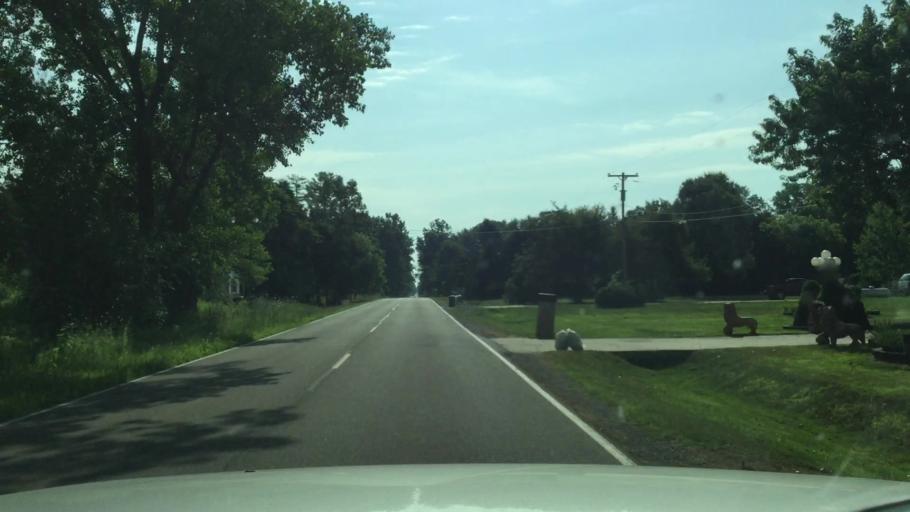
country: US
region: Michigan
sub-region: Genesee County
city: Montrose
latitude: 43.1333
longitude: -83.8522
